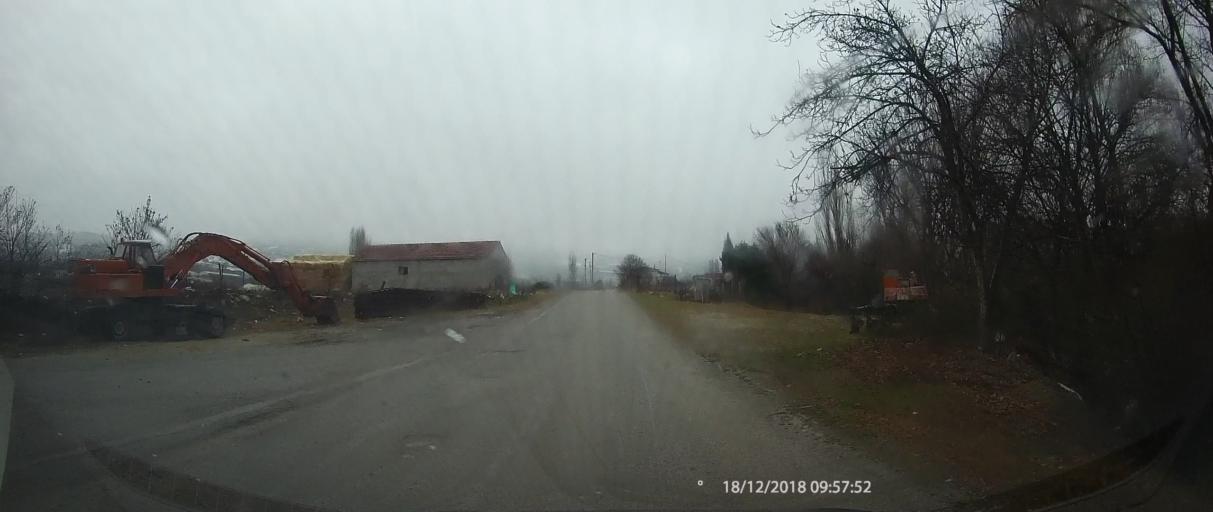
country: GR
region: Thessaly
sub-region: Nomos Larisis
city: Livadi
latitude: 40.0240
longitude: 22.2399
